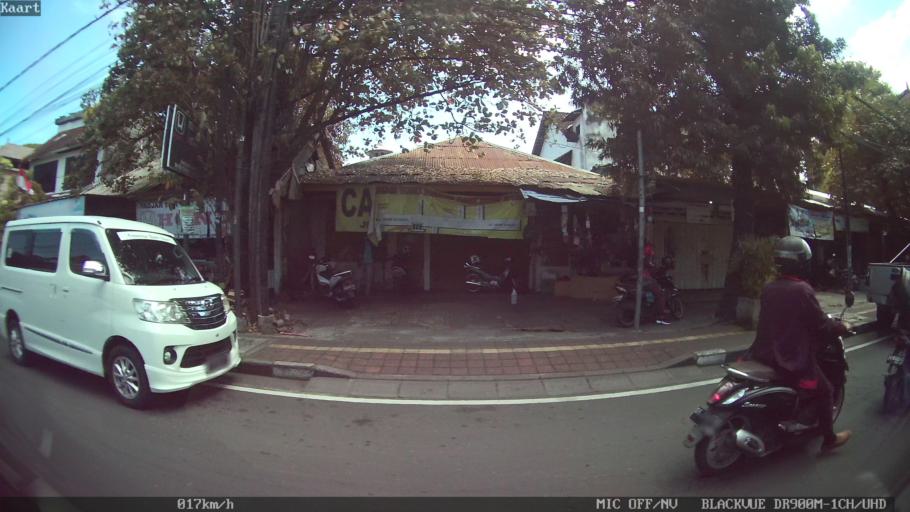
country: ID
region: Bali
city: Denpasar
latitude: -8.6589
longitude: 115.2096
